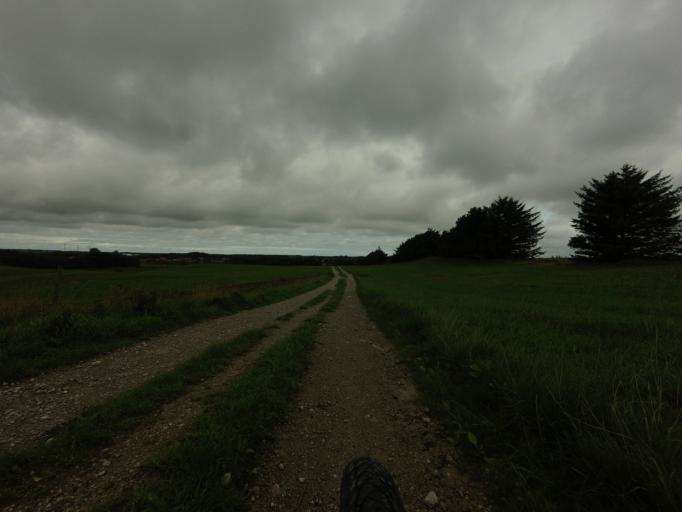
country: DK
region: North Denmark
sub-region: Hjorring Kommune
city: Hjorring
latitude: 57.4731
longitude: 9.9800
